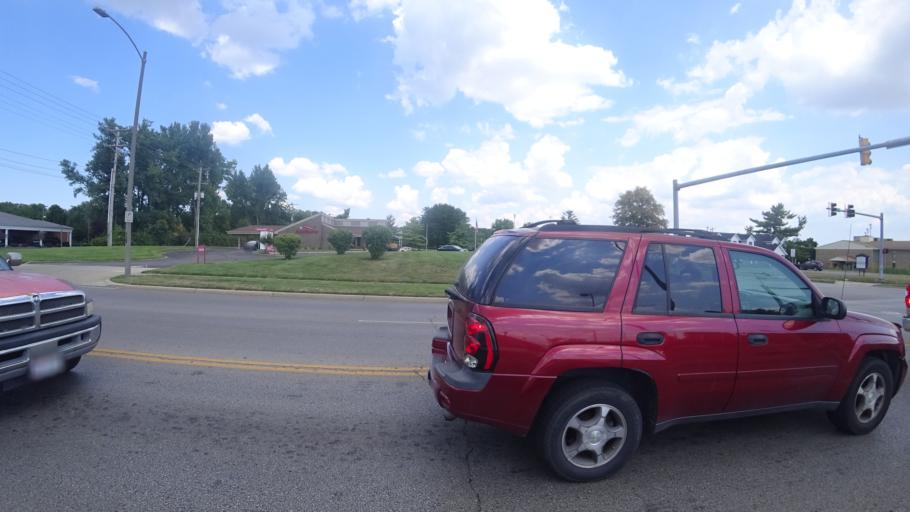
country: US
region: Ohio
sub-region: Butler County
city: Hamilton
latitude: 39.4245
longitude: -84.5850
